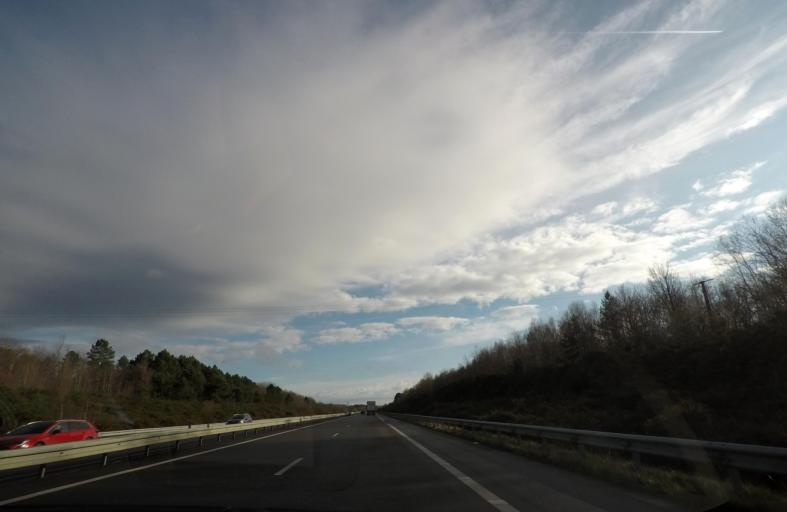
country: FR
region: Centre
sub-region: Departement du Loir-et-Cher
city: Villefranche-sur-Cher
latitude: 47.3101
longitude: 1.8353
